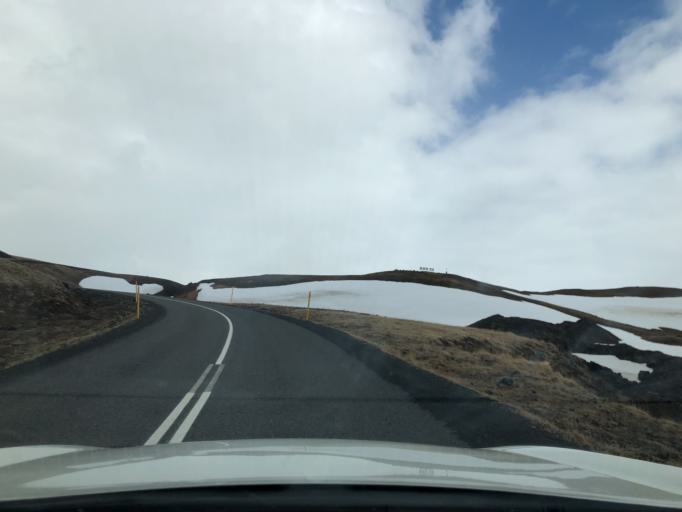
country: IS
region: Northeast
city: Laugar
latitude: 65.7087
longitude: -16.7712
